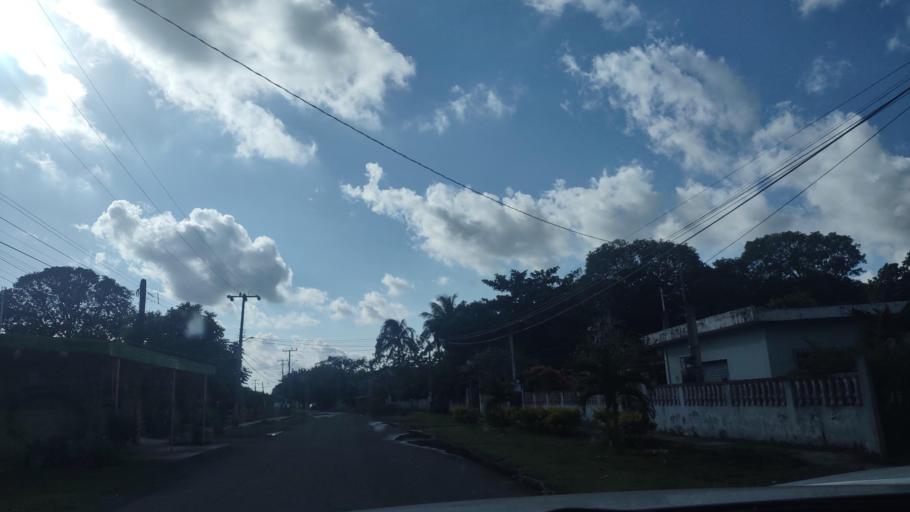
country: MX
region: Veracruz
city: El Tejar
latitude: 19.0710
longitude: -96.1653
